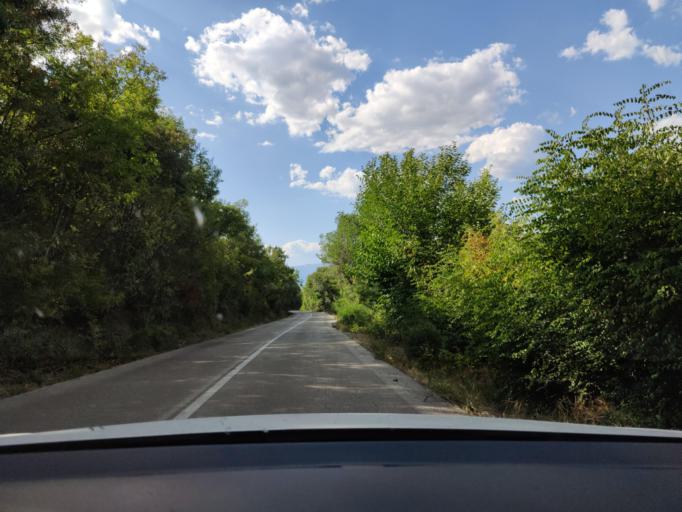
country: GR
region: Central Macedonia
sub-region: Nomos Serron
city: Chrysochorafa
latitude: 41.1644
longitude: 23.1827
